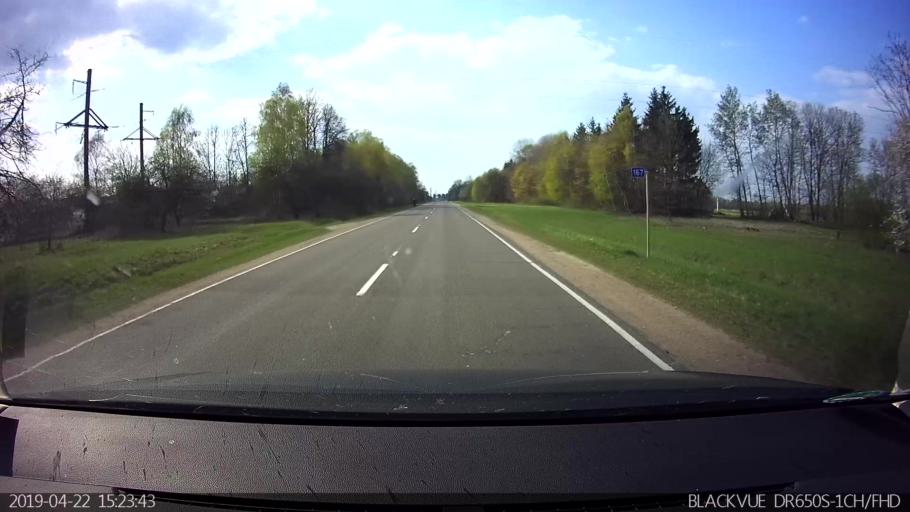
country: BY
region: Brest
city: Vysokaye
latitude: 52.3570
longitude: 23.4205
